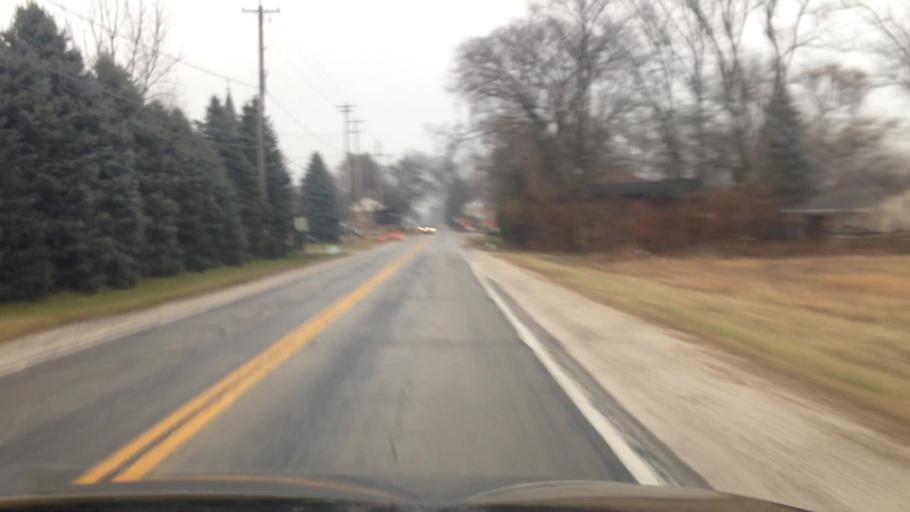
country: US
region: Wisconsin
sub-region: Washington County
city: Germantown
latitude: 43.2501
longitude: -88.1451
